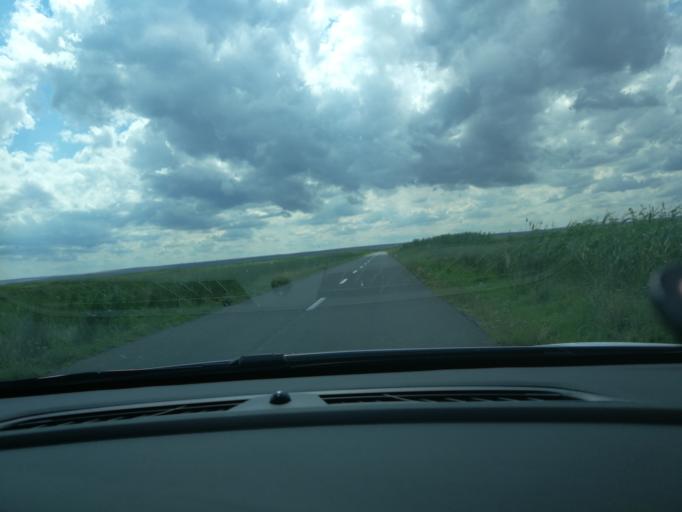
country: RO
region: Constanta
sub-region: Comuna Istria
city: Istria
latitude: 44.5373
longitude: 28.7462
